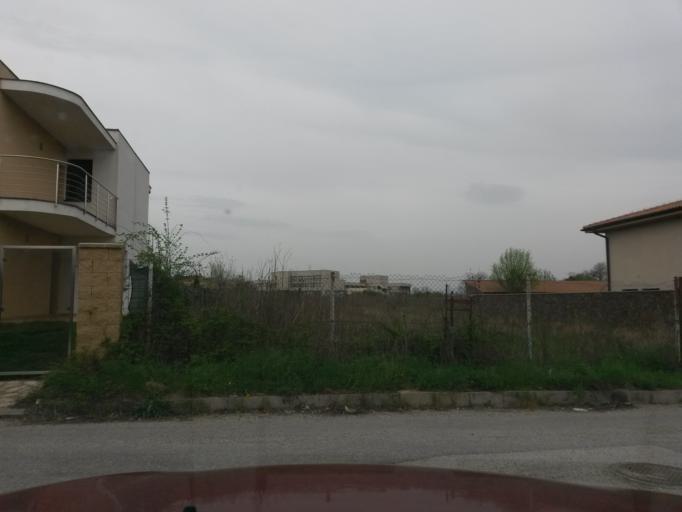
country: SK
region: Kosicky
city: Kosice
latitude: 48.7037
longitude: 21.2256
